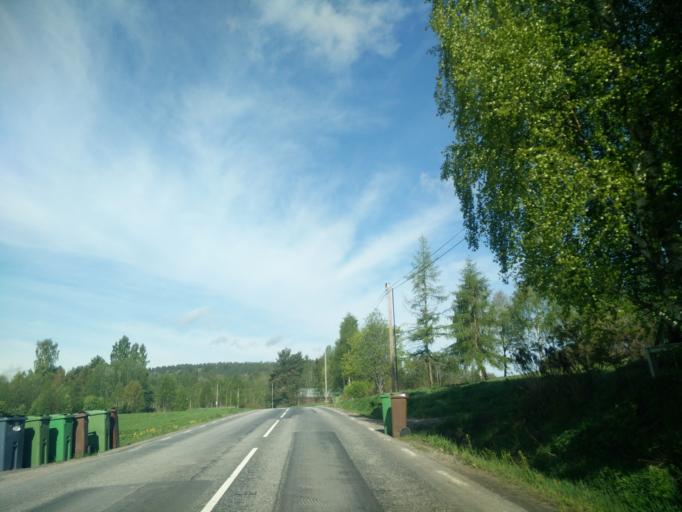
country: SE
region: Vaesternorrland
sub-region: Sundsvalls Kommun
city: Vi
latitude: 62.3098
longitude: 17.2429
